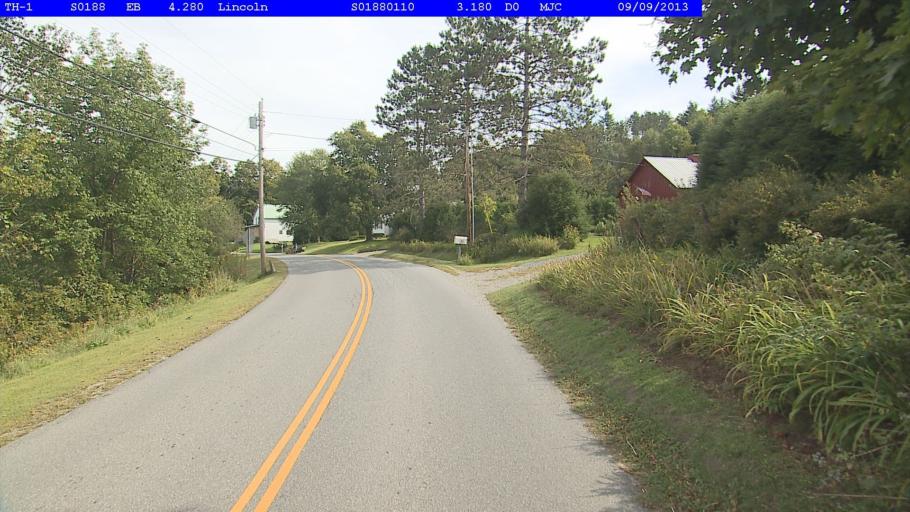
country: US
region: Vermont
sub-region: Addison County
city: Bristol
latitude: 44.0960
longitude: -72.9856
